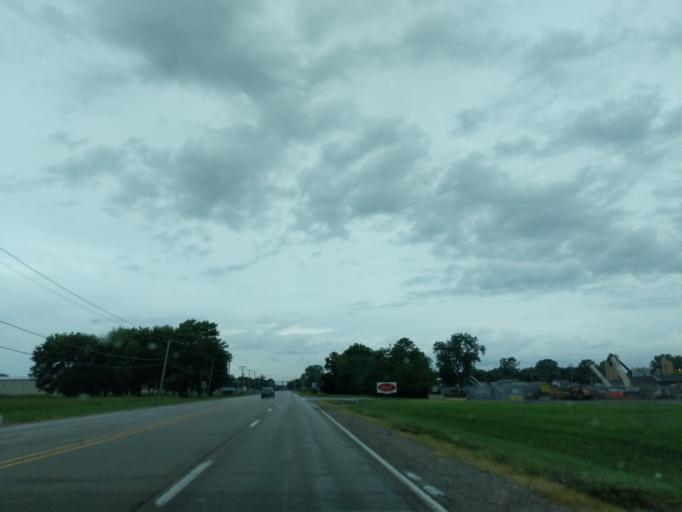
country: US
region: Illinois
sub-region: Saint Clair County
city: Fairmont City
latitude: 38.6591
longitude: -90.0751
